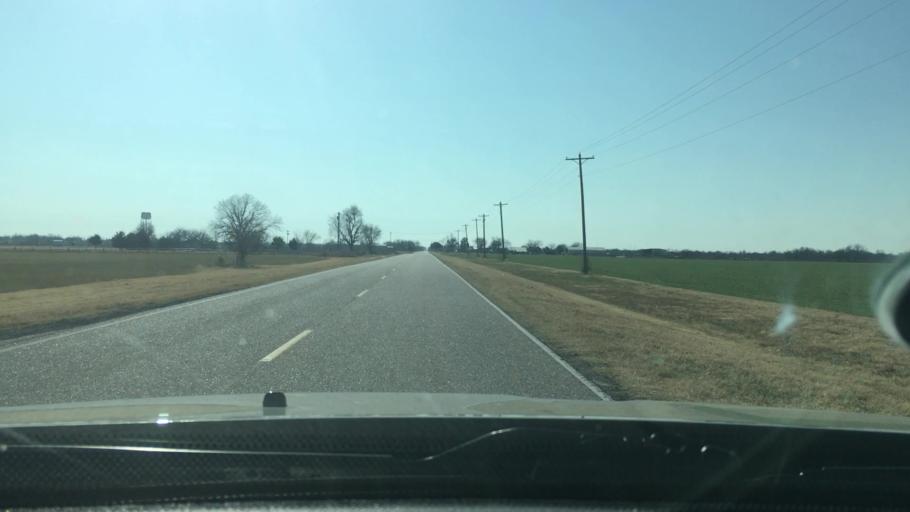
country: US
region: Oklahoma
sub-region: Garvin County
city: Stratford
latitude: 34.8183
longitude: -96.9677
